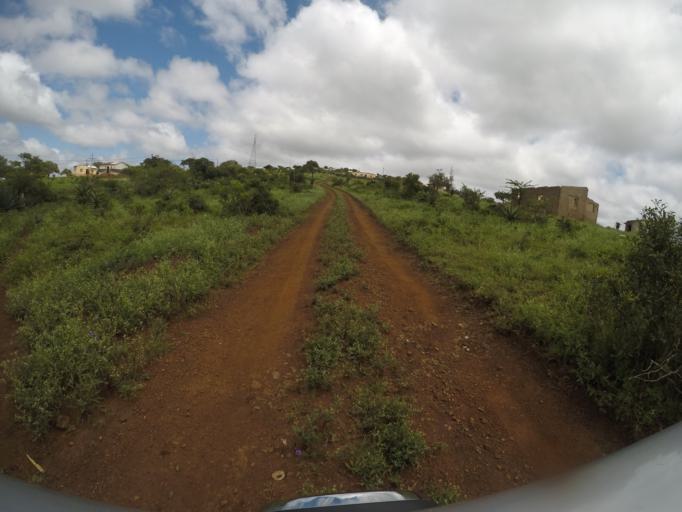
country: ZA
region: KwaZulu-Natal
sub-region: uThungulu District Municipality
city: Empangeni
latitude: -28.5769
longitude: 31.8307
